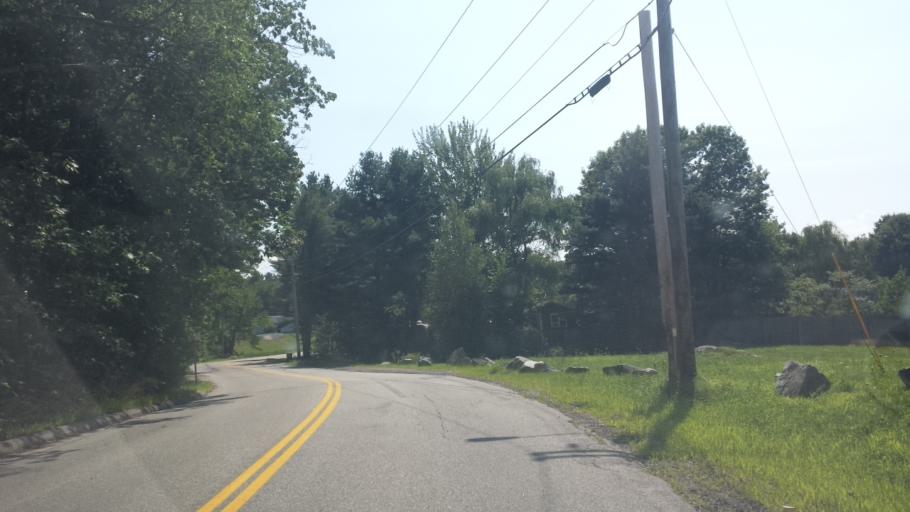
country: US
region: Maine
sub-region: York County
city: Biddeford
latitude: 43.4734
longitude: -70.4978
